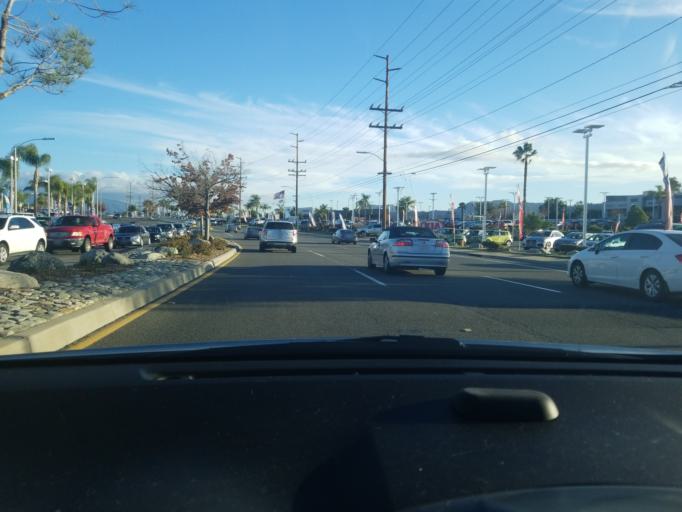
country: US
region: California
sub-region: Riverside County
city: Temecula
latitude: 33.5141
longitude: -117.1550
